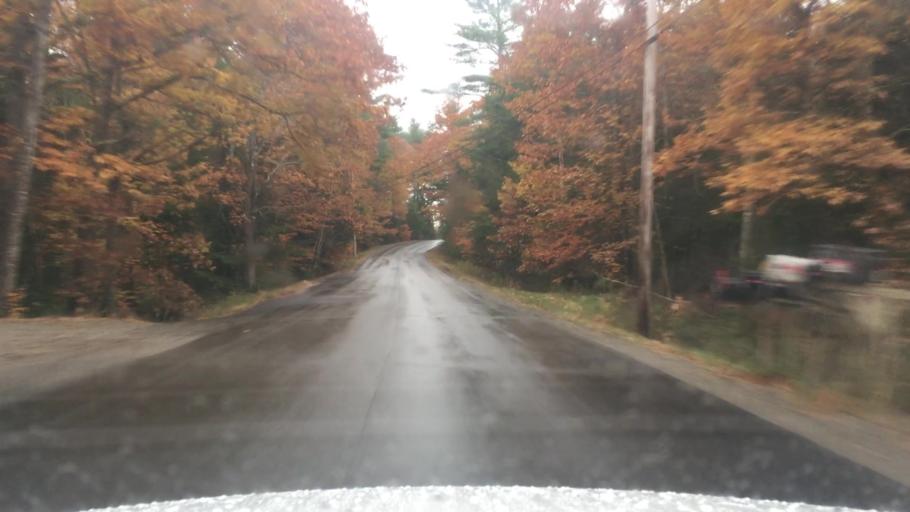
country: US
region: Maine
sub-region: Waldo County
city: Lincolnville
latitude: 44.3134
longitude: -69.0710
